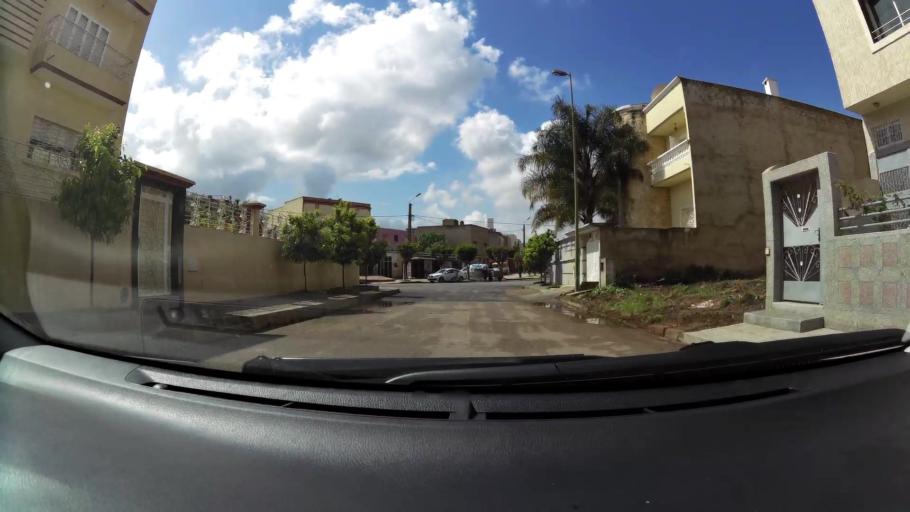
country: MA
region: Grand Casablanca
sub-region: Mediouna
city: Tit Mellil
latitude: 33.5536
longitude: -7.4865
